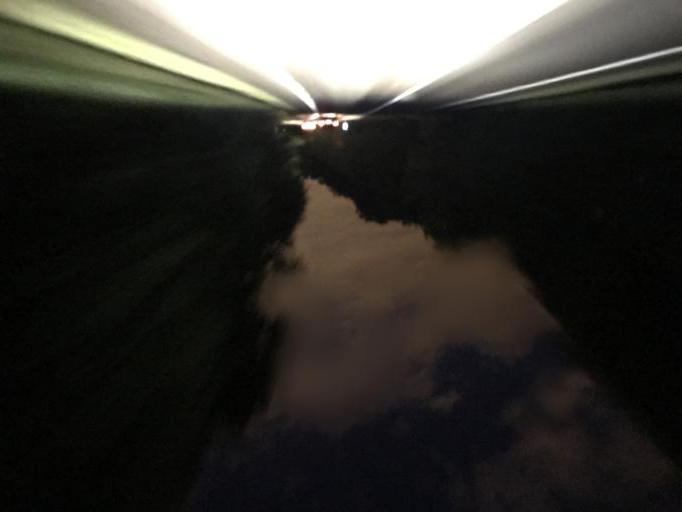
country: FR
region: Ile-de-France
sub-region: Departement des Yvelines
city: Le Mesnil-le-Roi
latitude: 48.9415
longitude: 2.1083
